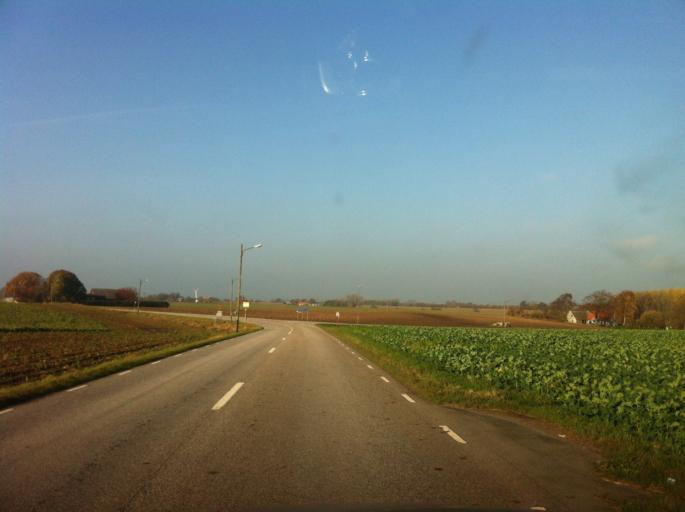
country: SE
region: Skane
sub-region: Helsingborg
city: Gantofta
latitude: 55.9741
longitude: 12.8155
